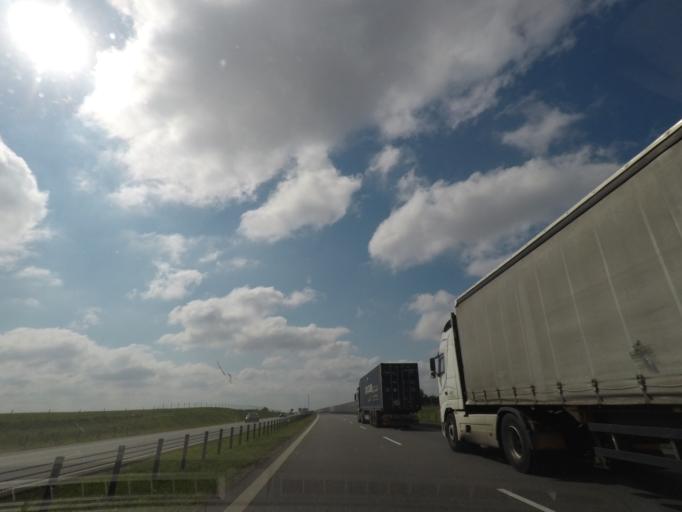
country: PL
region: Kujawsko-Pomorskie
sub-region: Powiat torunski
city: Lubicz Dolny
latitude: 53.1249
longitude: 18.7398
